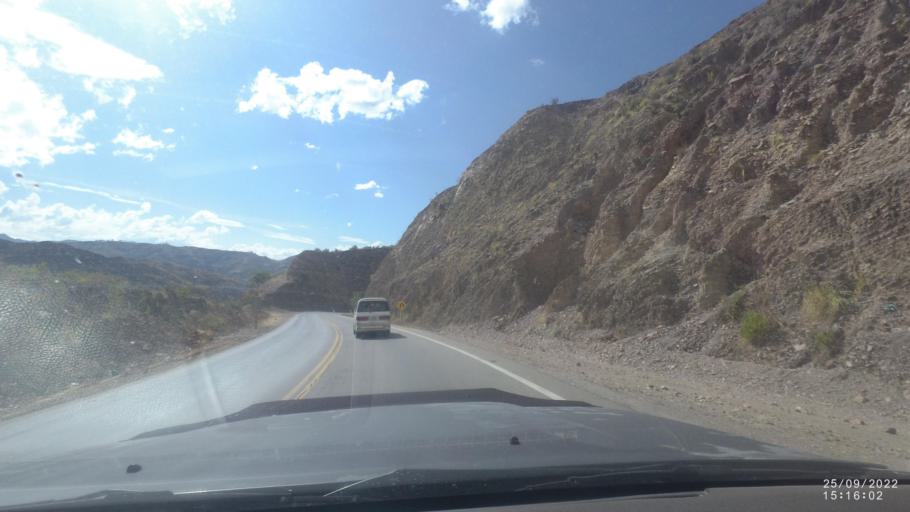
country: BO
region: Cochabamba
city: Irpa Irpa
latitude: -17.6287
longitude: -66.3919
